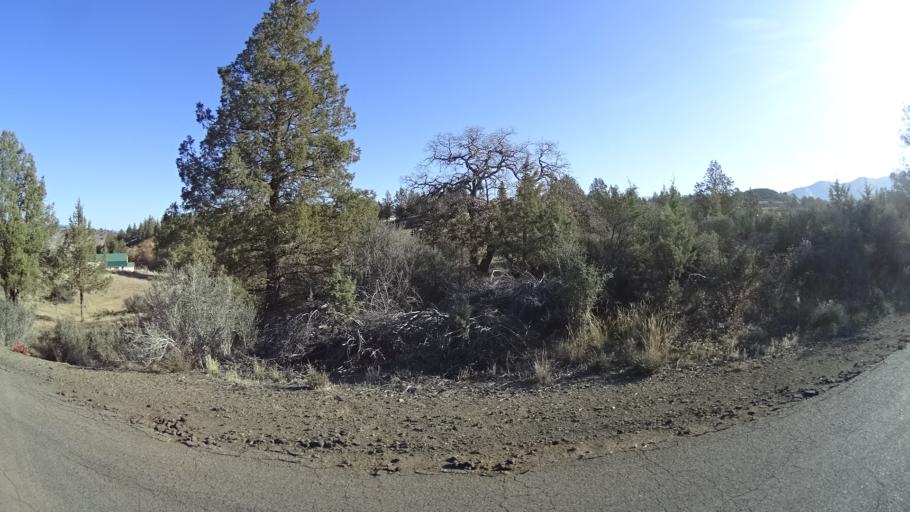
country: US
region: California
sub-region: Siskiyou County
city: Montague
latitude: 41.8813
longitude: -122.4527
